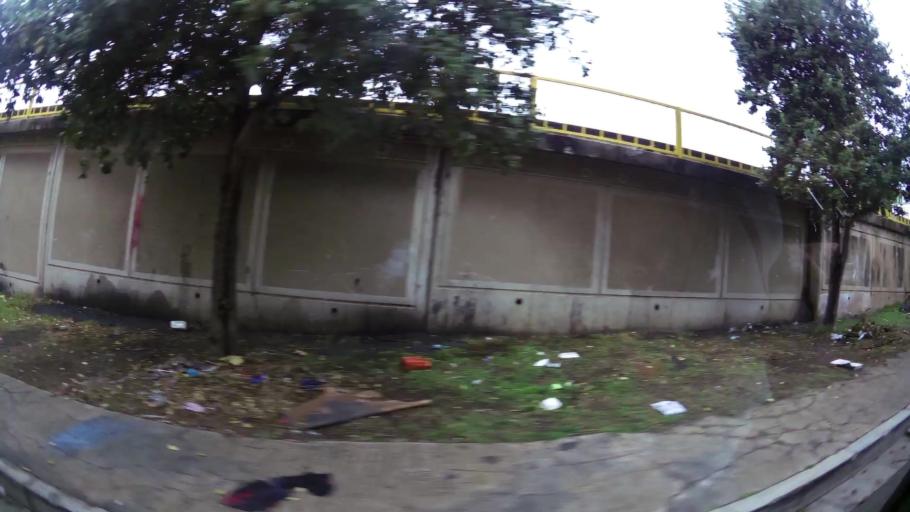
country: ZA
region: Eastern Cape
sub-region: Nelson Mandela Bay Metropolitan Municipality
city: Port Elizabeth
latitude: -33.9525
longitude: 25.6124
